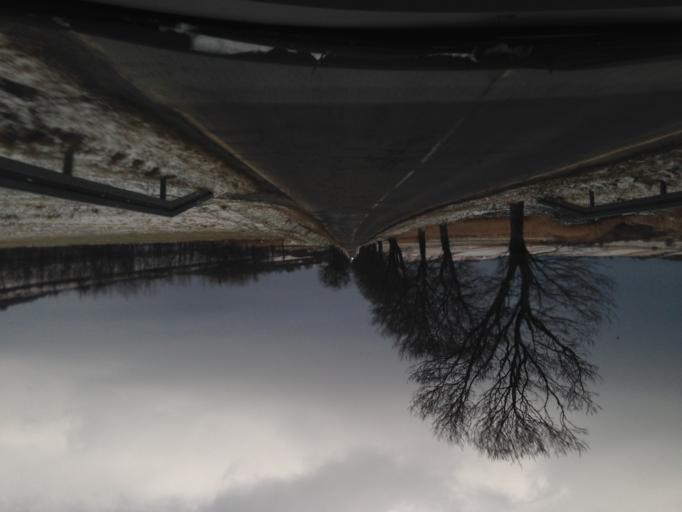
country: PL
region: Subcarpathian Voivodeship
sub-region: Powiat jasielski
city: Osiek Jasielski
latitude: 49.6108
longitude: 21.4863
